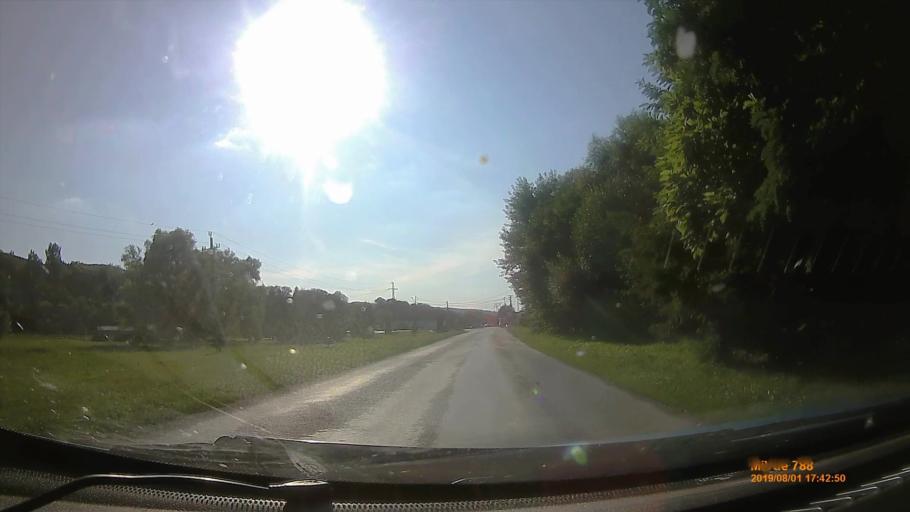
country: HU
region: Baranya
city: Sasd
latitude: 46.1911
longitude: 18.1559
